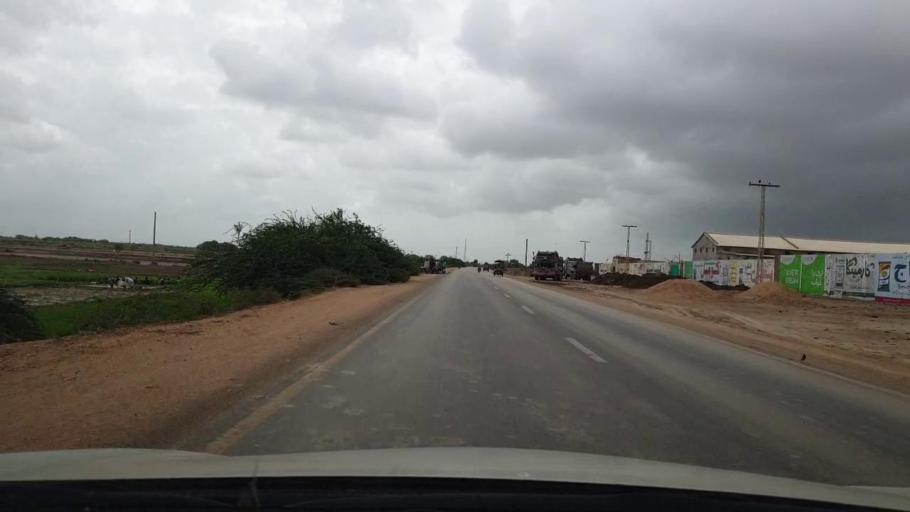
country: PK
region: Sindh
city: Mirpur Batoro
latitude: 24.6440
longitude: 68.4166
